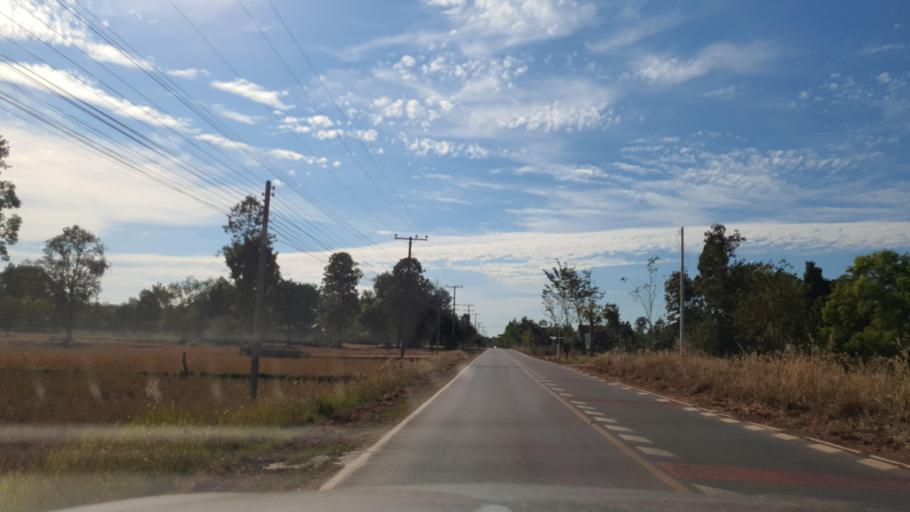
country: TH
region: Kalasin
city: Kuchinarai
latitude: 16.5428
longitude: 104.0905
